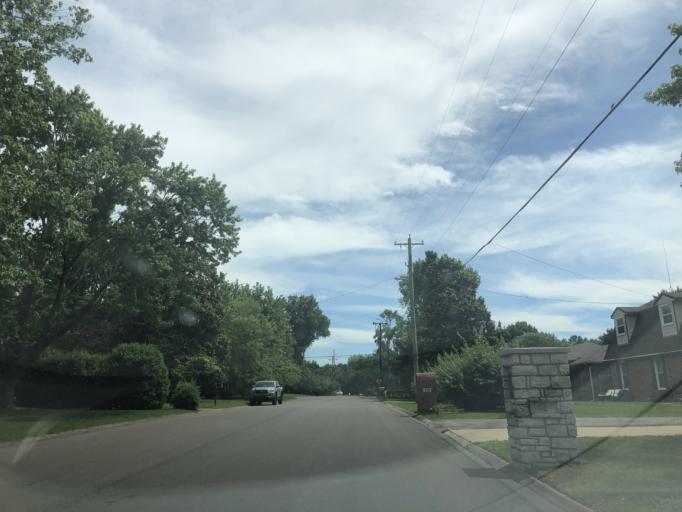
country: US
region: Tennessee
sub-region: Davidson County
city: Belle Meade
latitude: 36.0782
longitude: -86.9426
